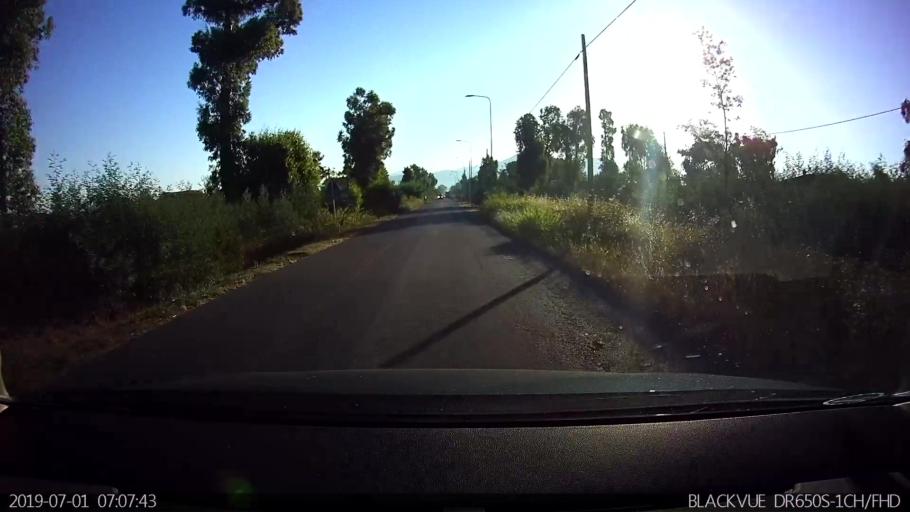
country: IT
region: Latium
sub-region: Provincia di Latina
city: Borgo Hermada
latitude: 41.2913
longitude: 13.1421
